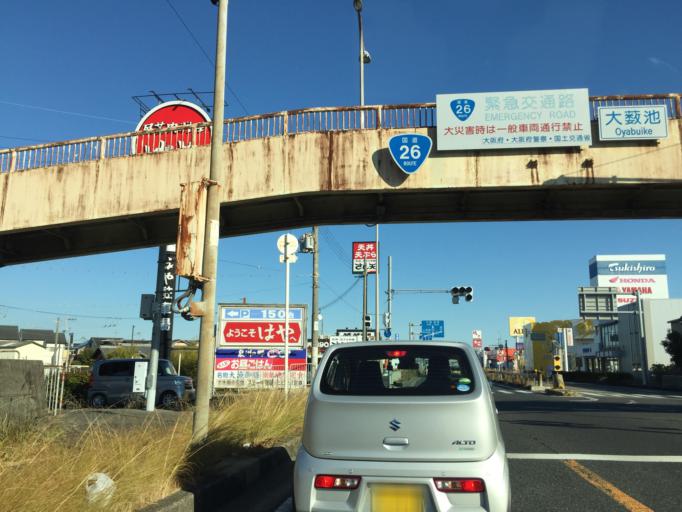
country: JP
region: Osaka
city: Kaizuka
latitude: 34.4196
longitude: 135.3379
